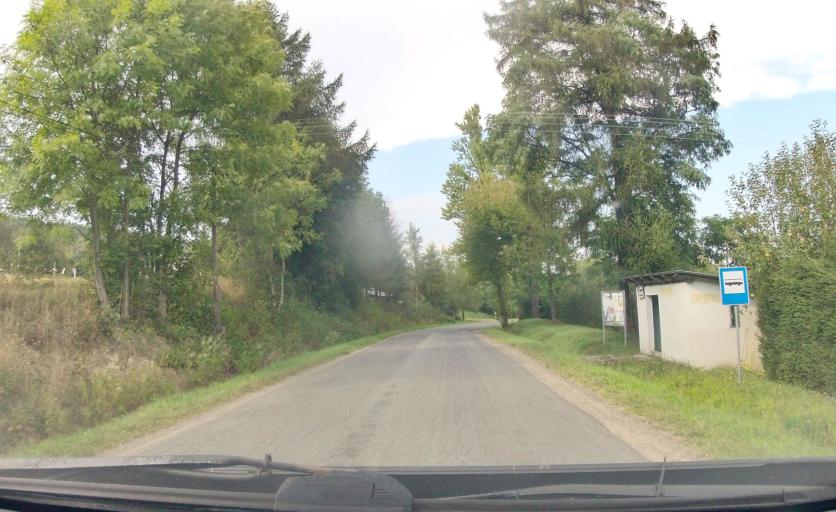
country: PL
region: Subcarpathian Voivodeship
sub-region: Powiat krosnienski
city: Dukla
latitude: 49.5241
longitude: 21.6151
